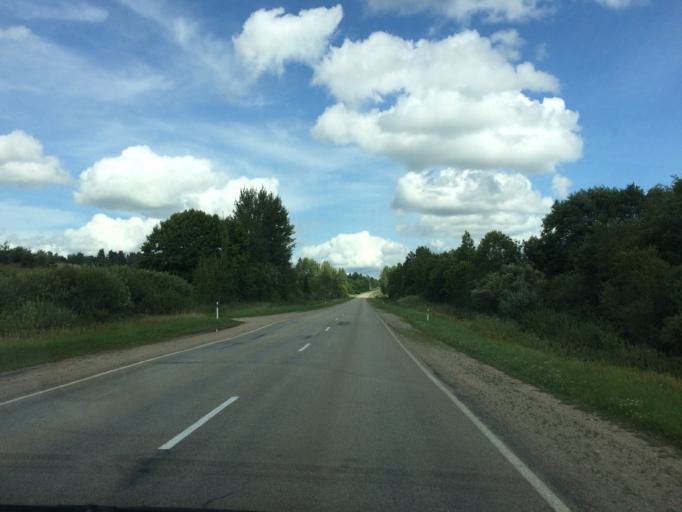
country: LV
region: Rezekne
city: Rezekne
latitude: 56.5731
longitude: 27.3744
